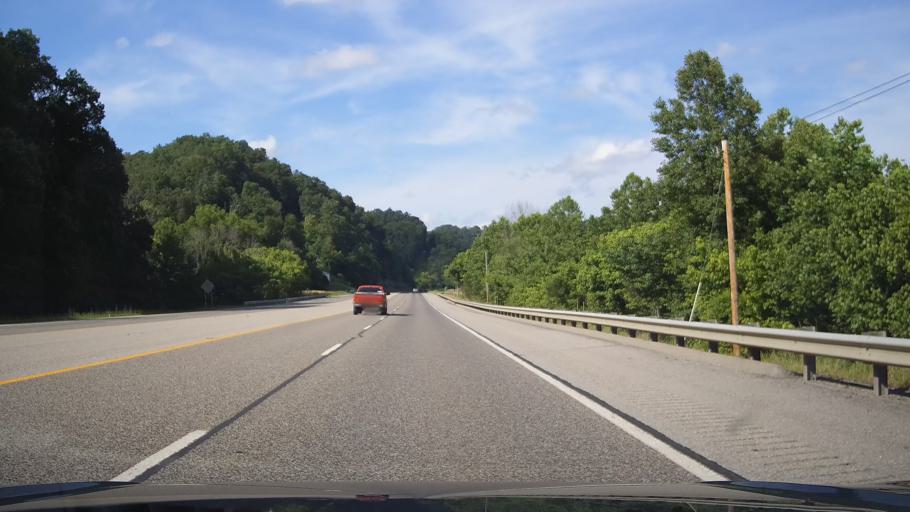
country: US
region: Kentucky
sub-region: Lawrence County
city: Louisa
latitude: 38.0143
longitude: -82.6599
